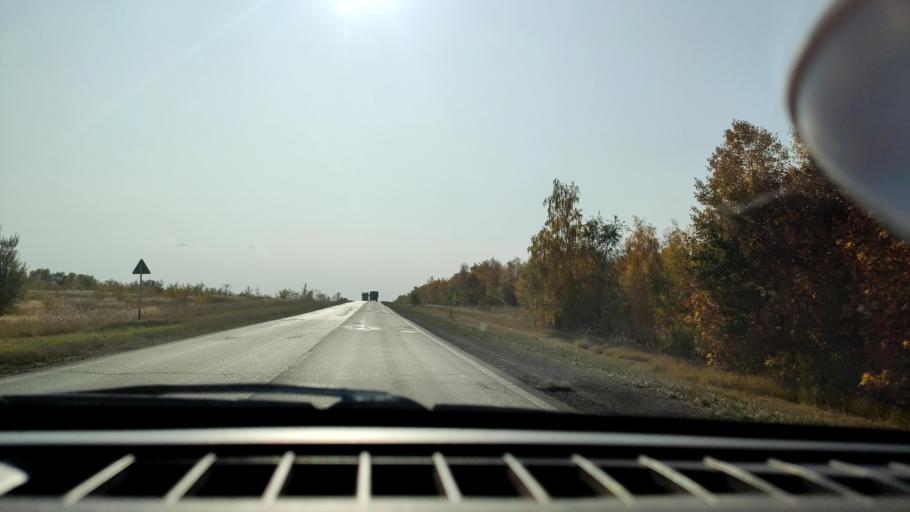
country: RU
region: Samara
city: Smyshlyayevka
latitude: 53.1180
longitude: 50.3636
